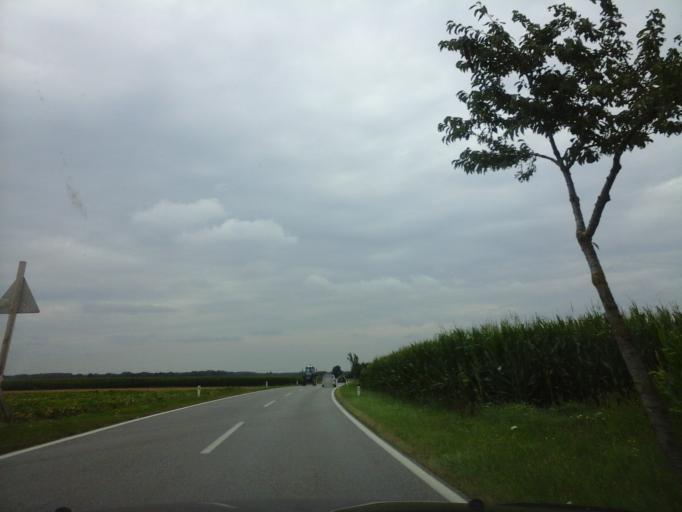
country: AT
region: Lower Austria
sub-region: Politischer Bezirk Ganserndorf
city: Orth an der Donau
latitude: 48.1553
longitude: 16.7358
